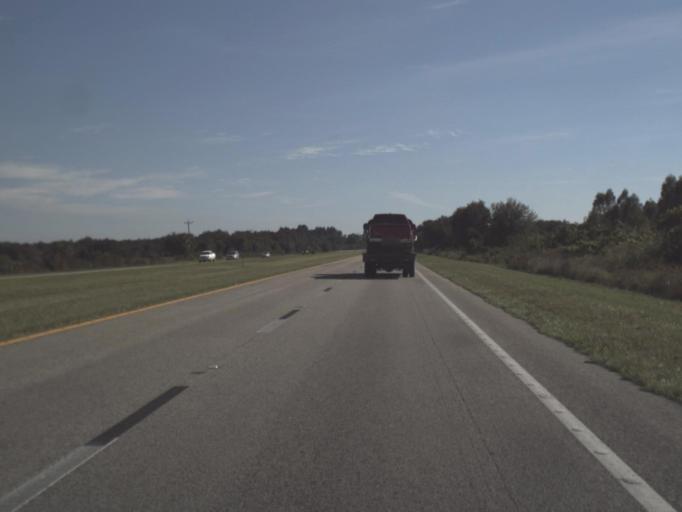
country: US
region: Florida
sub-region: Hendry County
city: Port LaBelle
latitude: 26.9772
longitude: -81.3198
